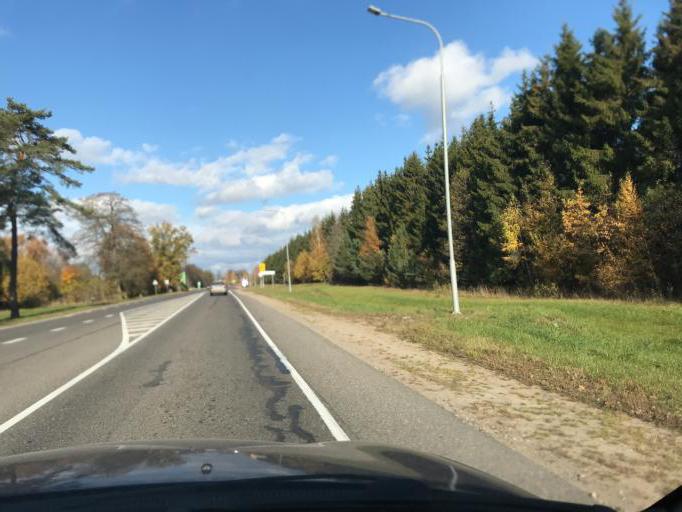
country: LT
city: Salcininkai
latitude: 54.2339
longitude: 25.3571
